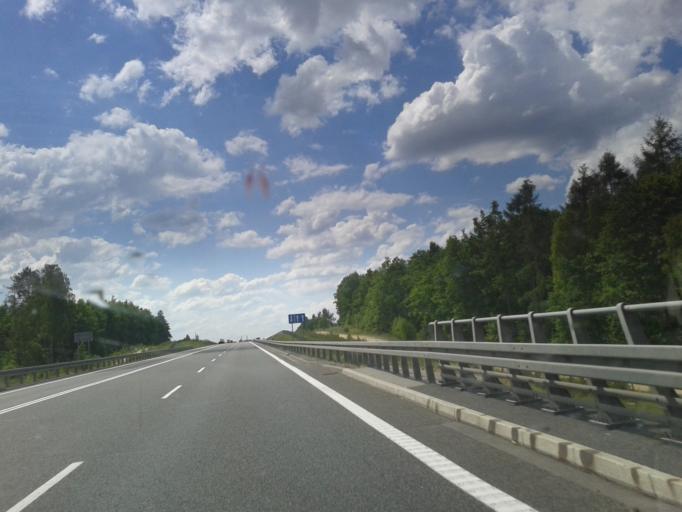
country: PL
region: Pomeranian Voivodeship
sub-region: Powiat chojnicki
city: Chojnice
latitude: 53.7016
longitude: 17.6335
